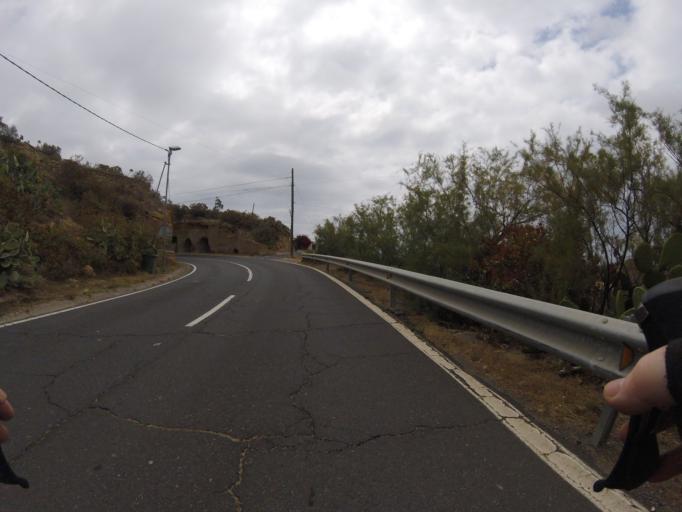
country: ES
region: Canary Islands
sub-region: Provincia de Santa Cruz de Tenerife
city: Guimar
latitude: 28.2766
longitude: -16.4128
